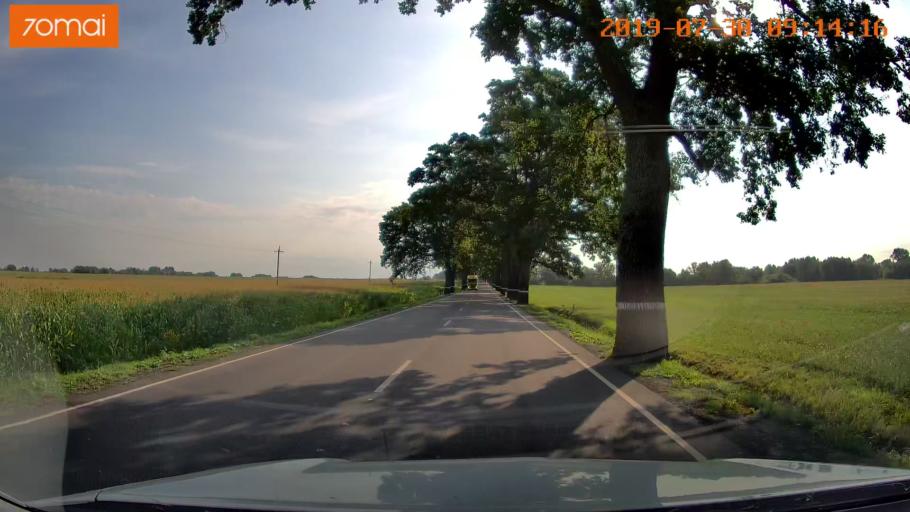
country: RU
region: Kaliningrad
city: Nesterov
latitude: 54.6283
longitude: 22.5144
